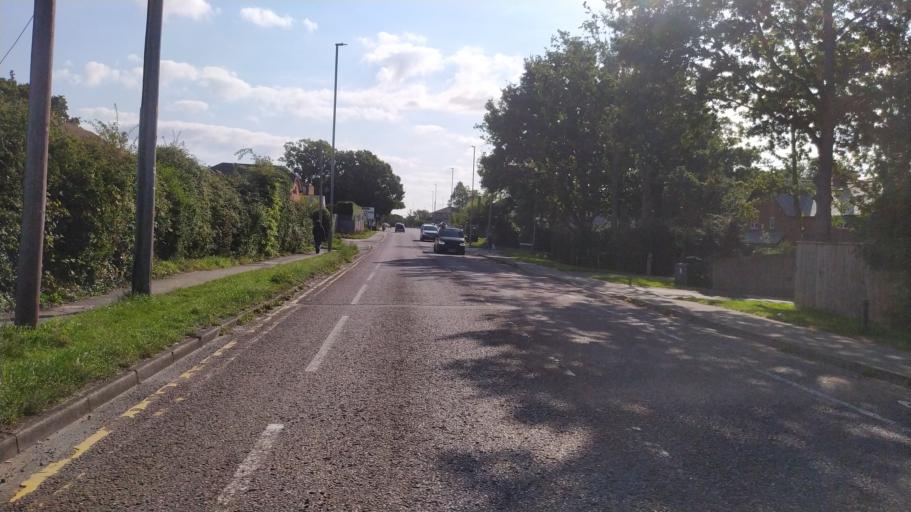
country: GB
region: England
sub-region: Poole
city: Poole
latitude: 50.7390
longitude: -2.0321
